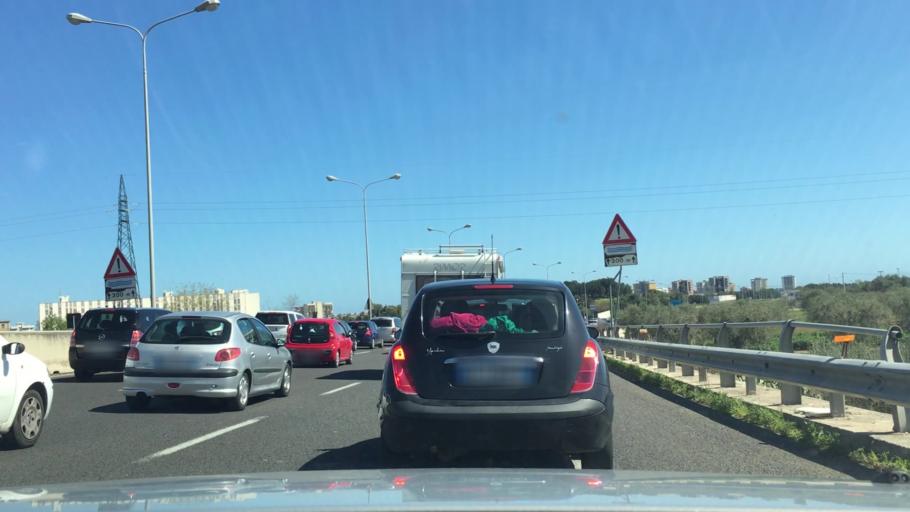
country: IT
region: Apulia
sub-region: Provincia di Bari
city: Triggiano
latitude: 41.0967
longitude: 16.8997
